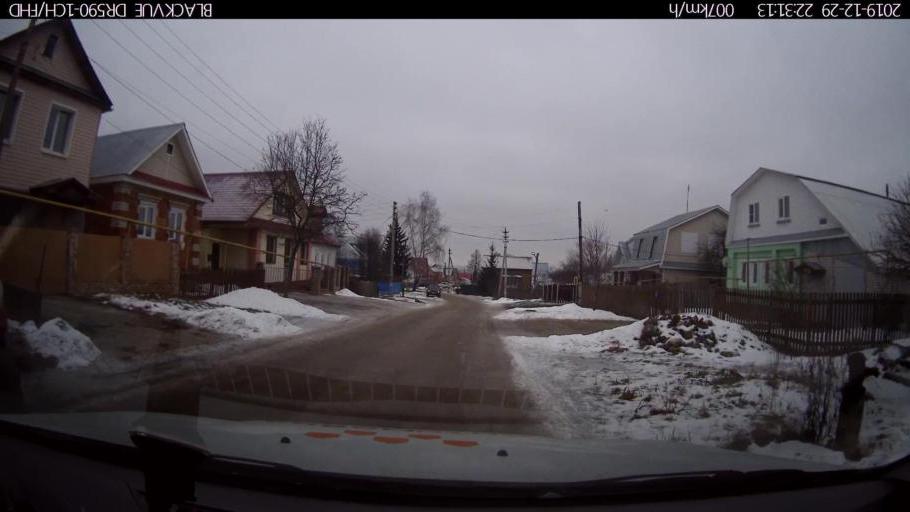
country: RU
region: Nizjnij Novgorod
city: Afonino
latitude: 56.2036
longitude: 43.9860
